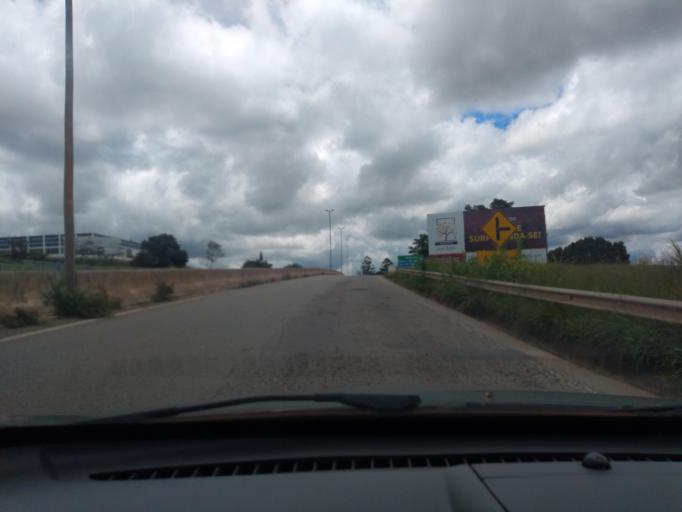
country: BR
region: Minas Gerais
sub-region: Lavras
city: Lavras
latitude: -21.2343
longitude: -45.0361
